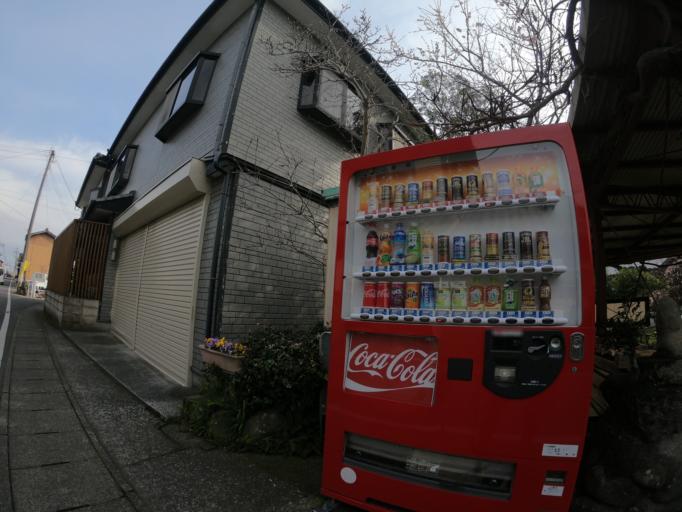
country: JP
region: Nagasaki
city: Shimabara
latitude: 32.6673
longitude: 130.3075
